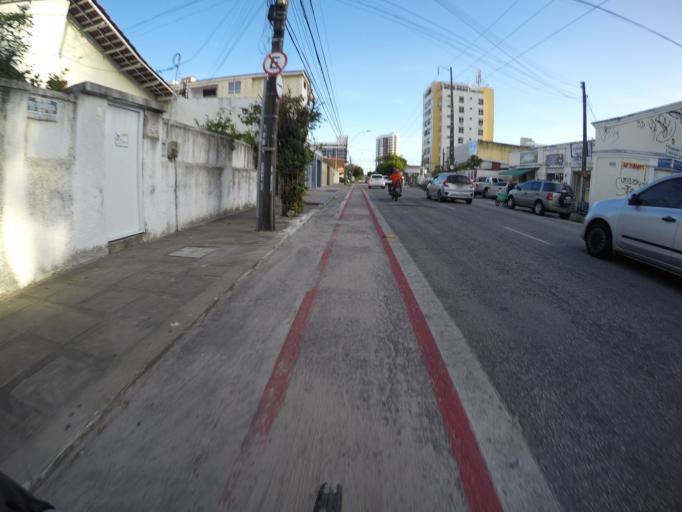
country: BR
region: Ceara
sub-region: Fortaleza
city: Fortaleza
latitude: -3.7436
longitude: -38.5118
